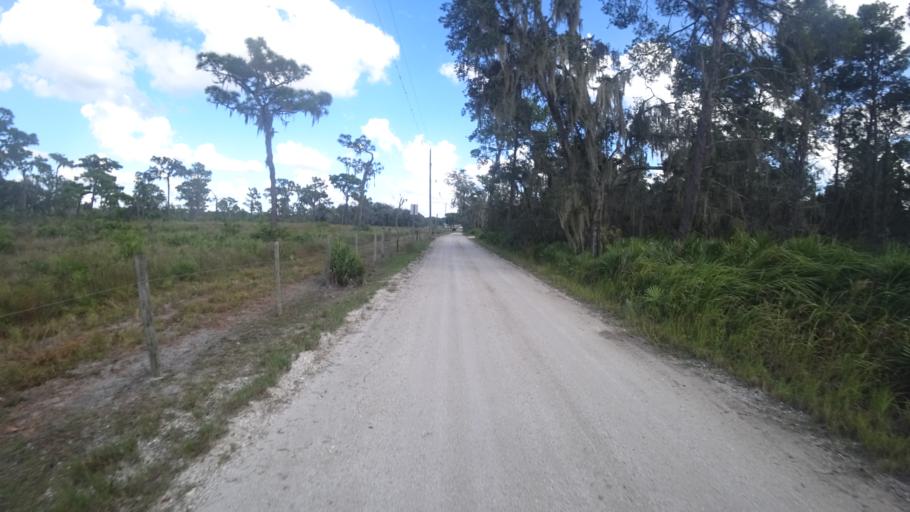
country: US
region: Florida
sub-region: Hillsborough County
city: Wimauma
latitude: 27.4373
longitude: -82.1475
